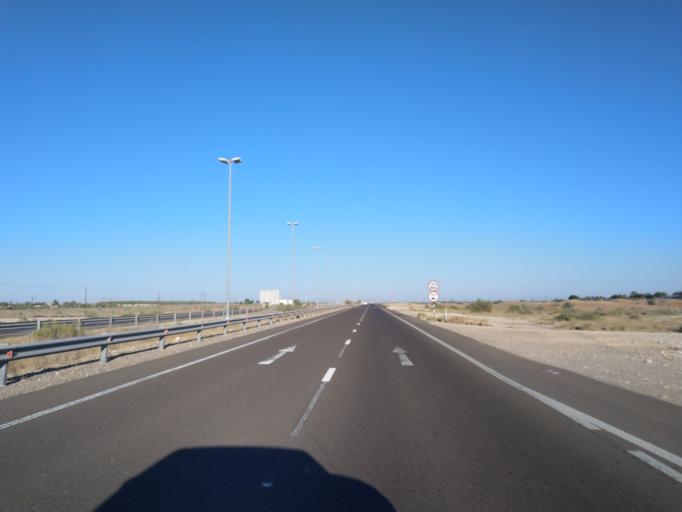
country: OM
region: Al Buraimi
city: Al Buraymi
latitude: 24.5386
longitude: 55.6104
